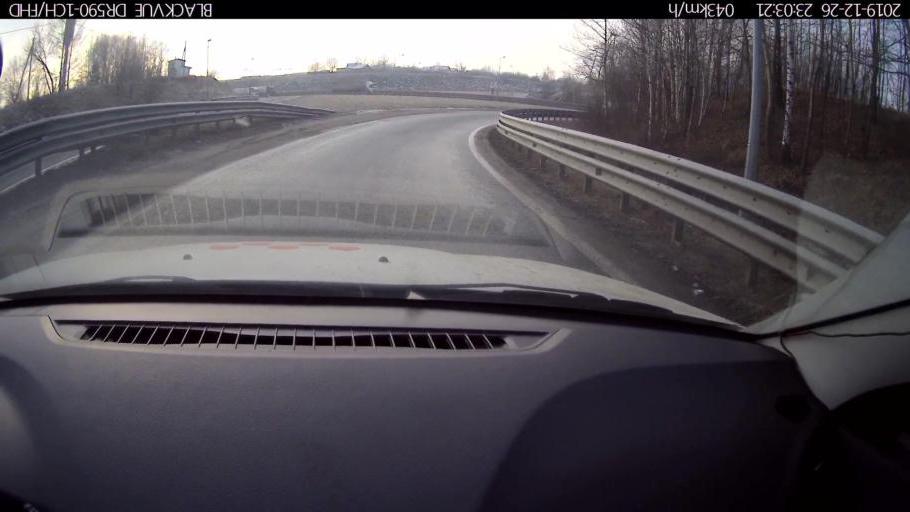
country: RU
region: Nizjnij Novgorod
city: Burevestnik
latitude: 56.1718
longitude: 43.7505
